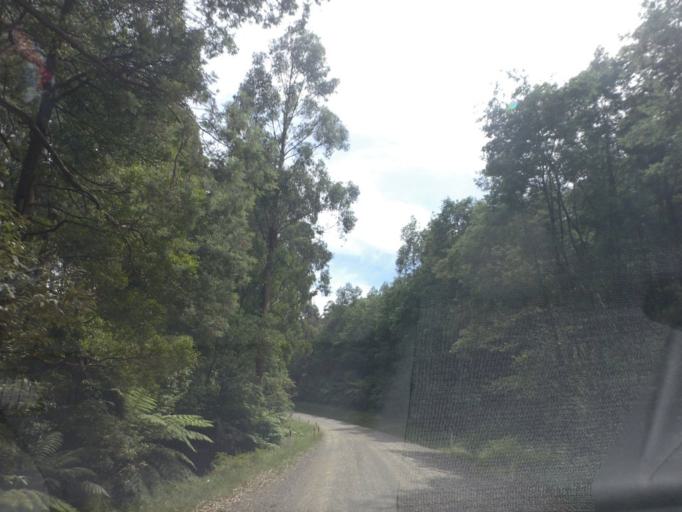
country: AU
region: Victoria
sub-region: Yarra Ranges
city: Healesville
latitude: -37.5362
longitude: 145.5138
